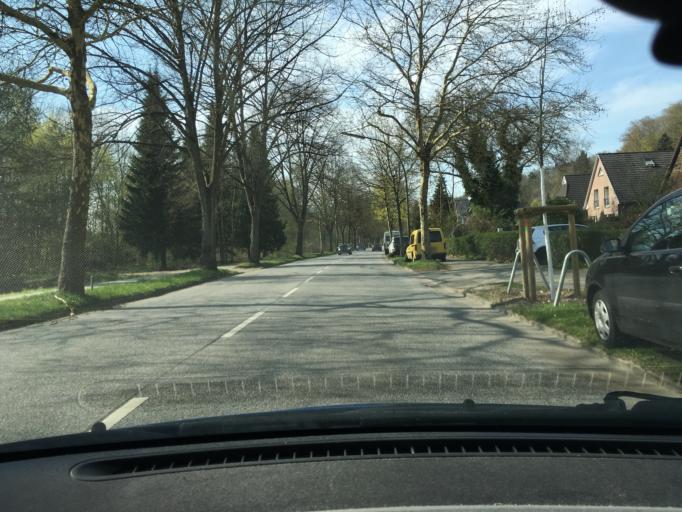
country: DE
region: Hamburg
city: Bergedorf
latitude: 53.4744
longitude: 10.2520
